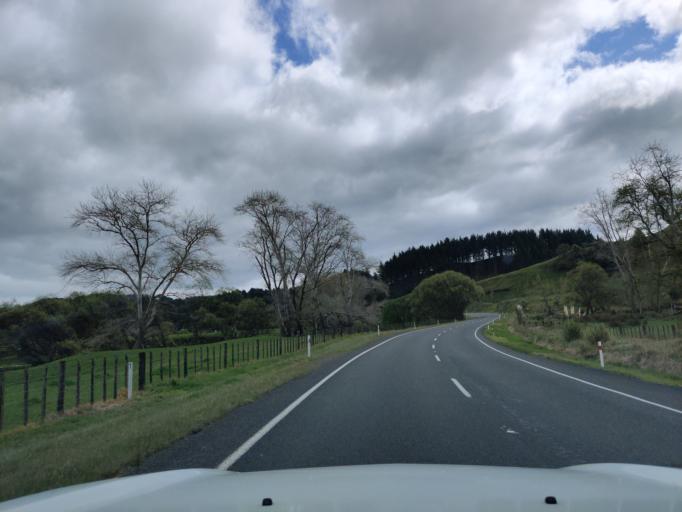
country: NZ
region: Manawatu-Wanganui
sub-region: Wanganui District
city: Wanganui
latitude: -39.8484
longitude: 175.1345
